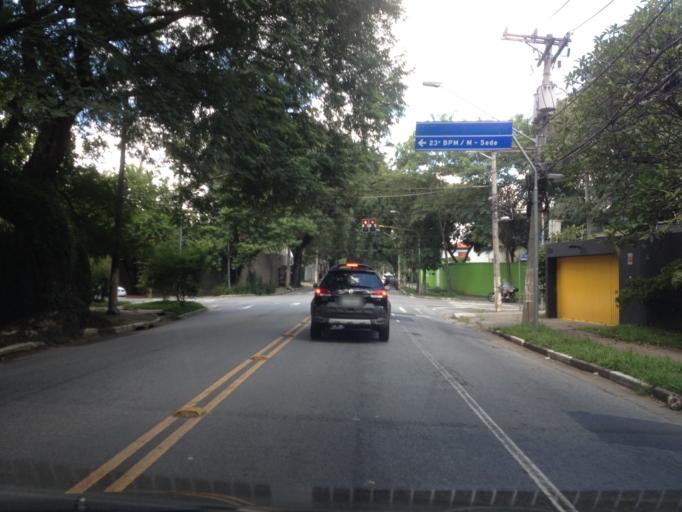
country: BR
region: Sao Paulo
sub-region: Sao Paulo
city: Sao Paulo
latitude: -23.5505
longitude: -46.7076
